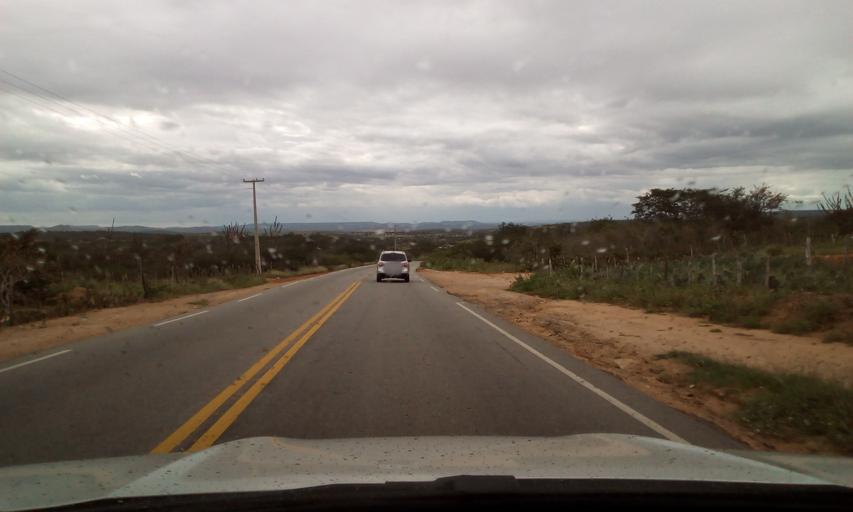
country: BR
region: Paraiba
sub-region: Picui
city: Picui
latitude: -6.5714
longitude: -36.2717
